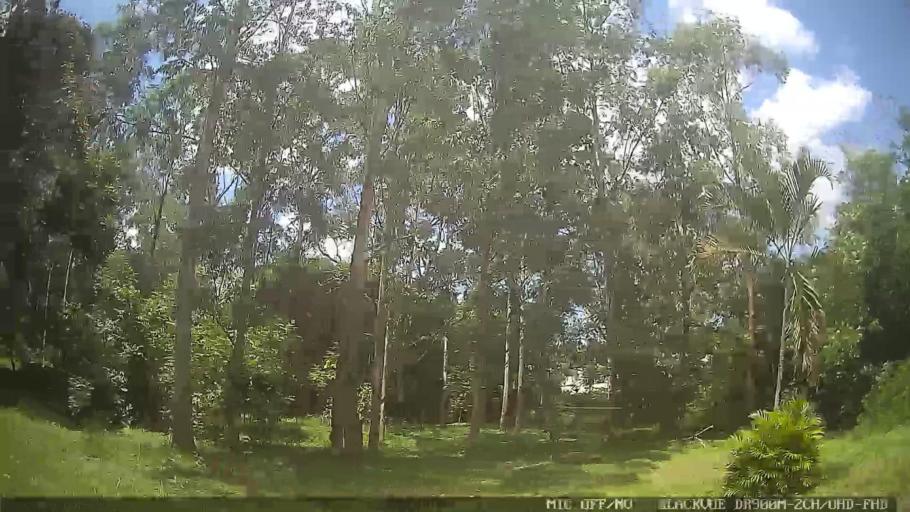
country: BR
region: Sao Paulo
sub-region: Jacarei
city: Jacarei
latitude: -23.3014
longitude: -46.0171
